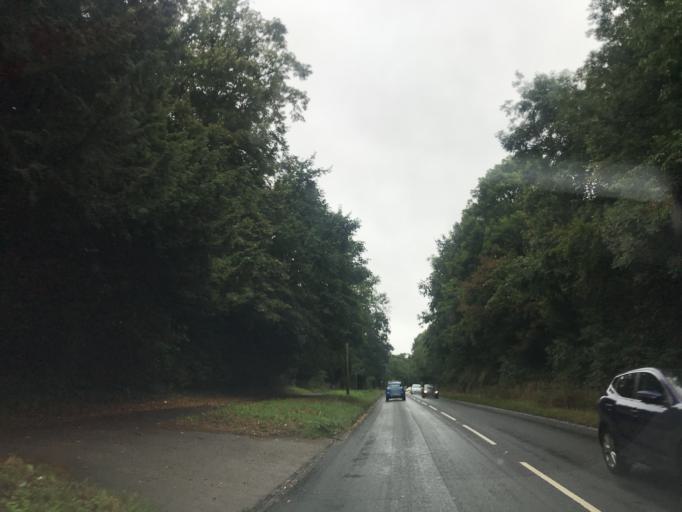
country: GB
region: England
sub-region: Buckinghamshire
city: Aylesbury
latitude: 51.8060
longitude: -0.8370
